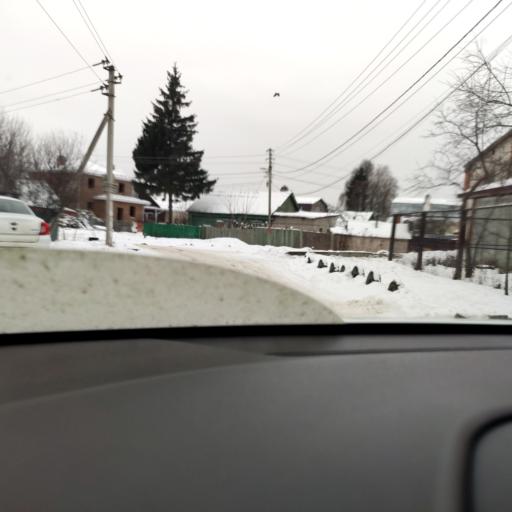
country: RU
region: Tatarstan
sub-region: Gorod Kazan'
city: Kazan
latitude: 55.8637
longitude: 49.0572
